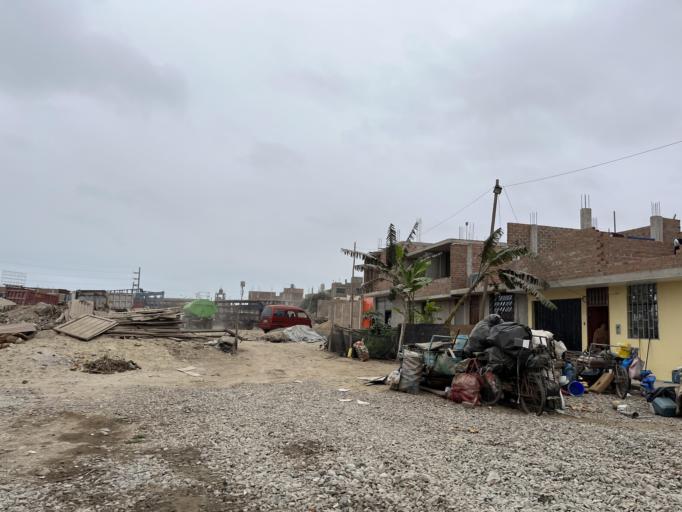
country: PE
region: La Libertad
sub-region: Provincia de Trujillo
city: Trujillo
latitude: -8.1289
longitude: -79.0193
